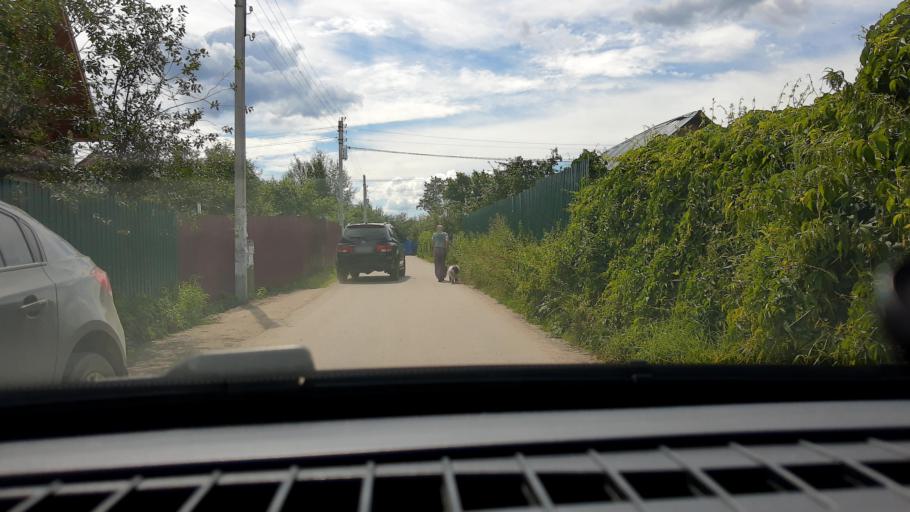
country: RU
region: Nizjnij Novgorod
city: Gorbatovka
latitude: 56.2504
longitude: 43.8131
